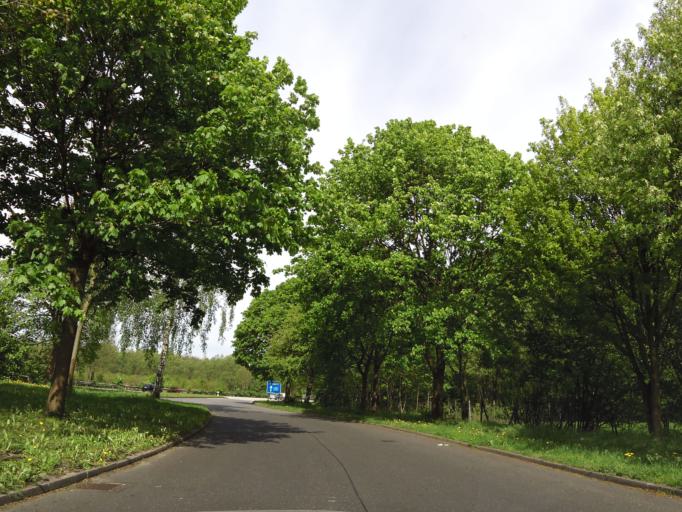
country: DE
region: Schleswig-Holstein
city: Kummerfeld
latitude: 53.7038
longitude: 9.7739
